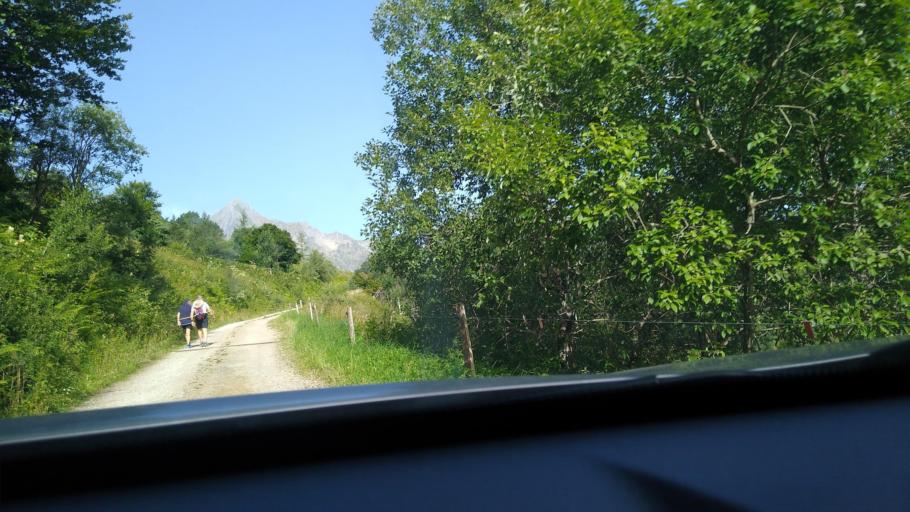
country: FR
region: Midi-Pyrenees
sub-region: Departement de l'Ariege
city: Saint-Girons
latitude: 42.7885
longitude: 1.1453
